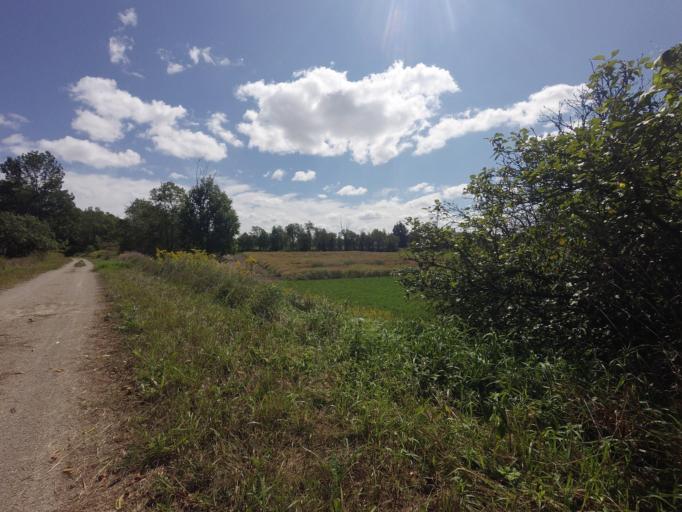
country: CA
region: Ontario
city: Orangeville
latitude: 43.7901
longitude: -80.2605
